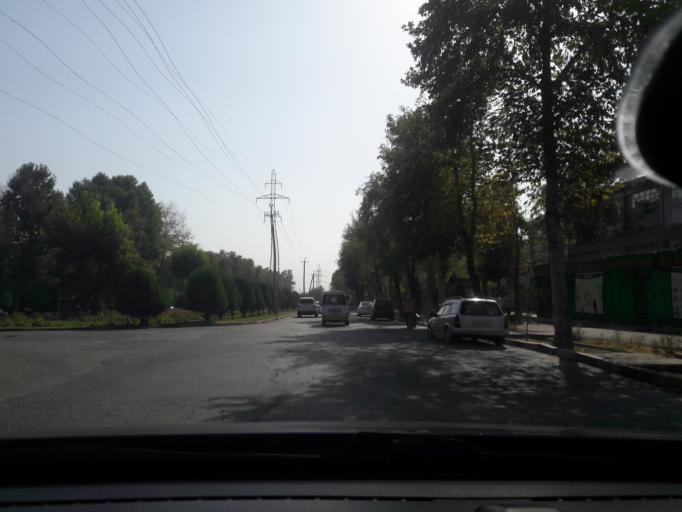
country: TJ
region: Dushanbe
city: Dushanbe
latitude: 38.5163
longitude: 68.7540
